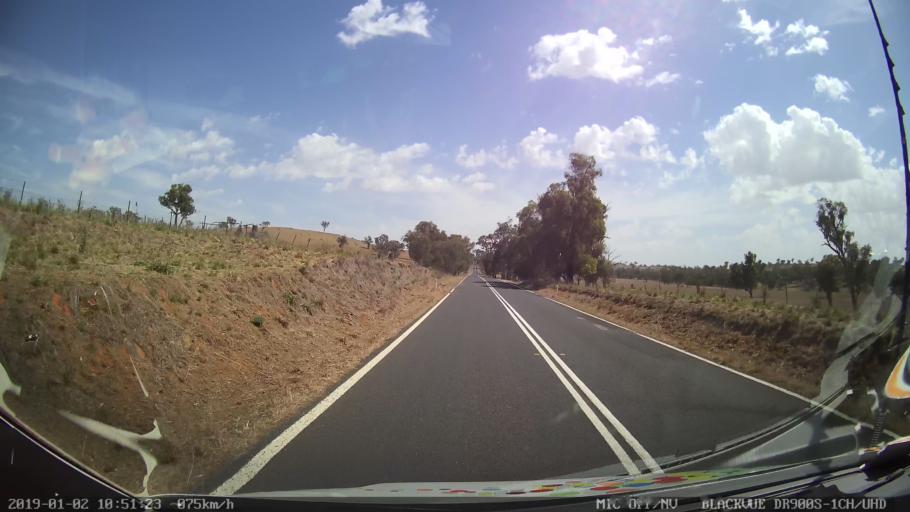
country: AU
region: New South Wales
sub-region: Cootamundra
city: Cootamundra
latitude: -34.7008
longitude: 148.2758
